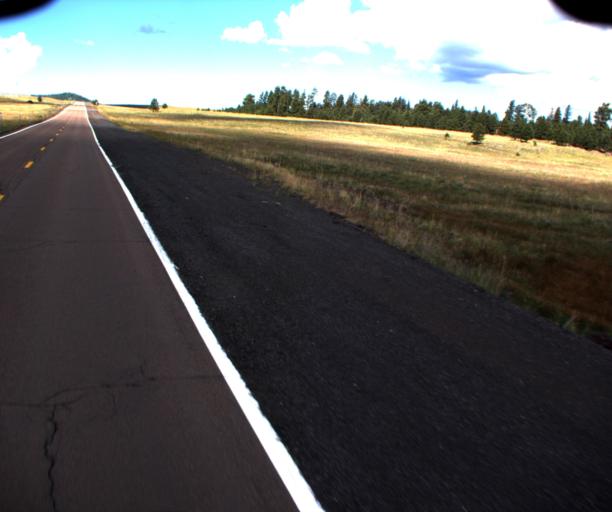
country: US
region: Arizona
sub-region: Apache County
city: Eagar
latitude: 34.0537
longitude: -109.5180
